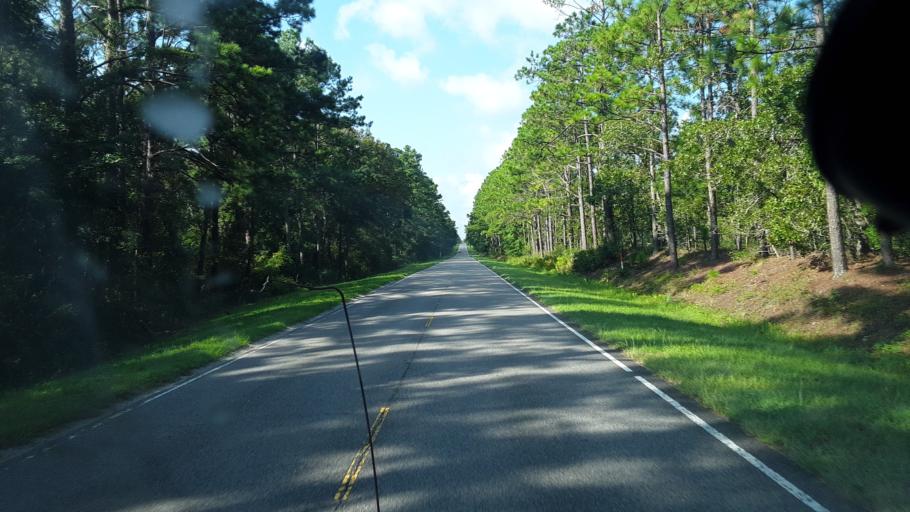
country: US
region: North Carolina
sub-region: Brunswick County
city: Boiling Spring Lakes
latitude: 34.0421
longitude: -78.0051
